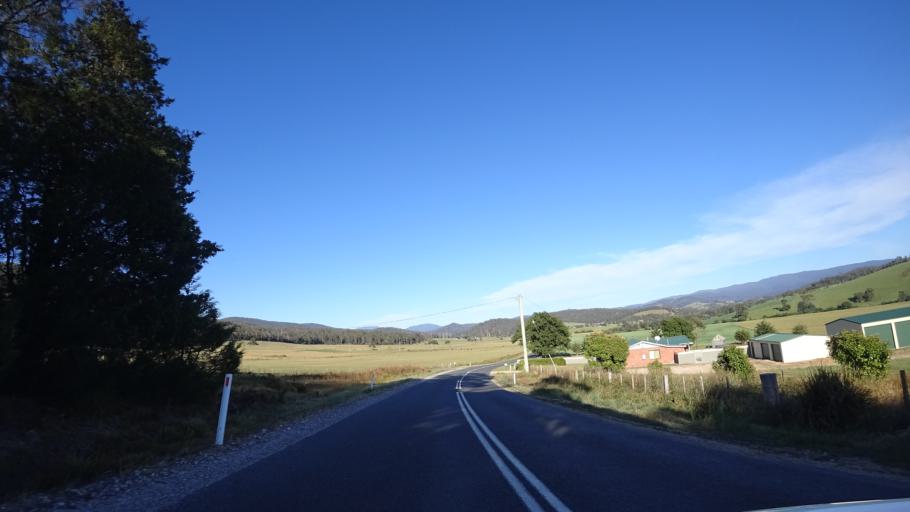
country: AU
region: Tasmania
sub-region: Break O'Day
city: St Helens
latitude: -41.2730
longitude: 148.1139
